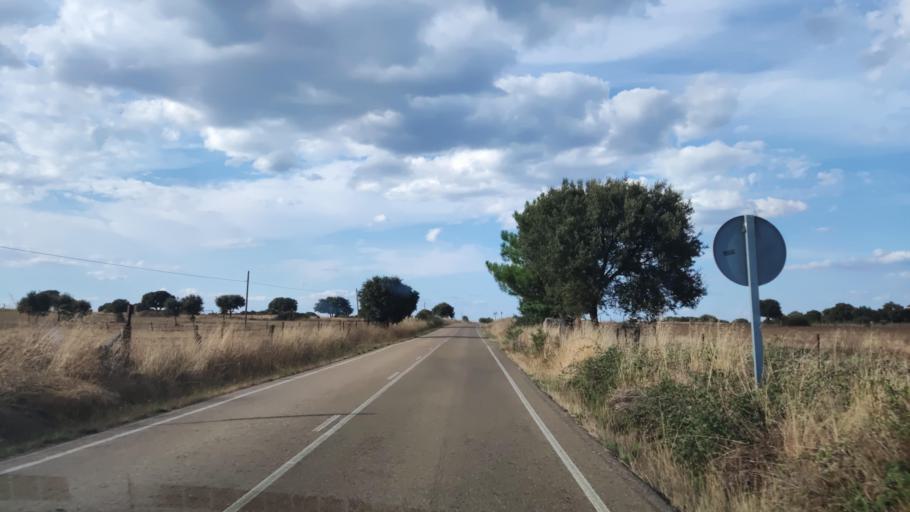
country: ES
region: Castille and Leon
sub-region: Provincia de Salamanca
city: Martiago
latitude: 40.4610
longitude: -6.4901
